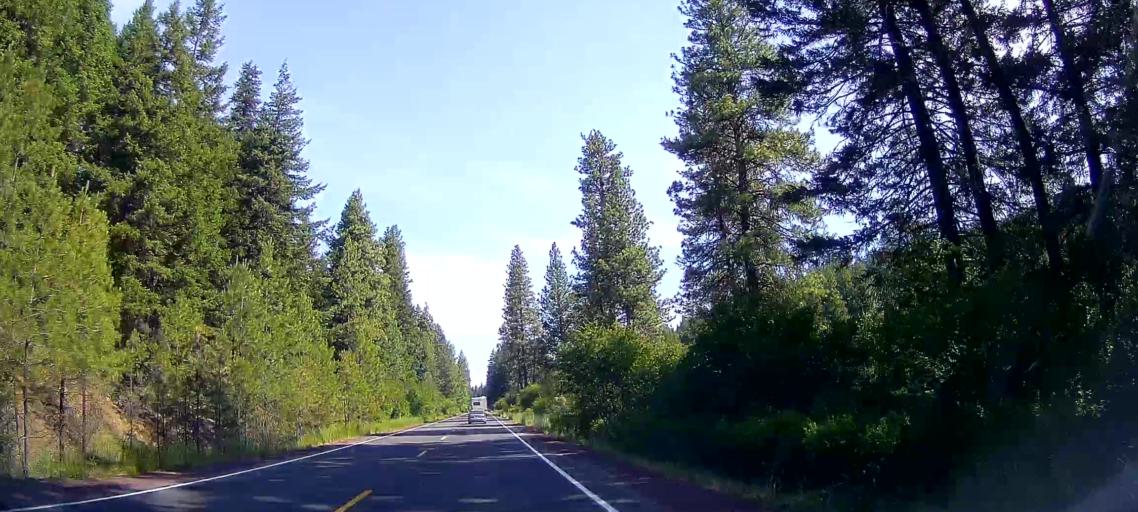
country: US
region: Oregon
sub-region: Jefferson County
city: Warm Springs
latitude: 45.0383
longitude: -121.5105
